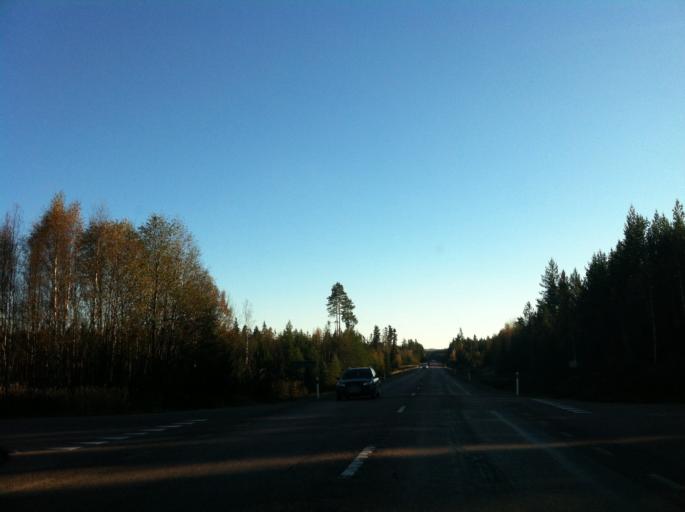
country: SE
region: Dalarna
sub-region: Rattviks Kommun
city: Raettvik
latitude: 60.8220
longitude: 15.2547
